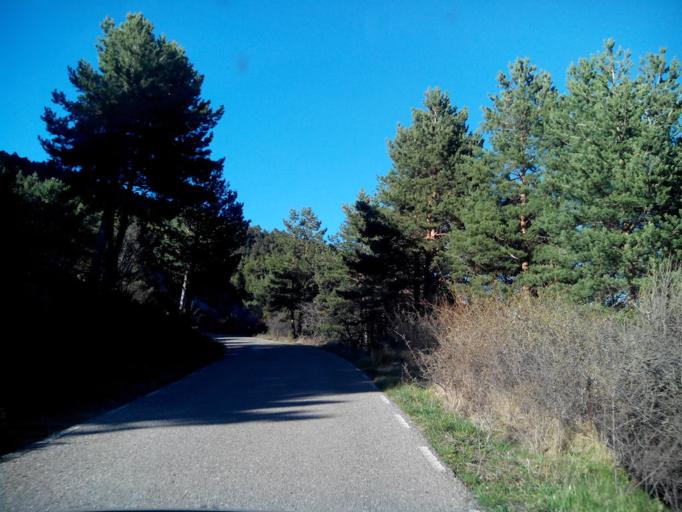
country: ES
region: Catalonia
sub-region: Provincia de Barcelona
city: Saldes
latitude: 42.2283
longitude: 1.7238
